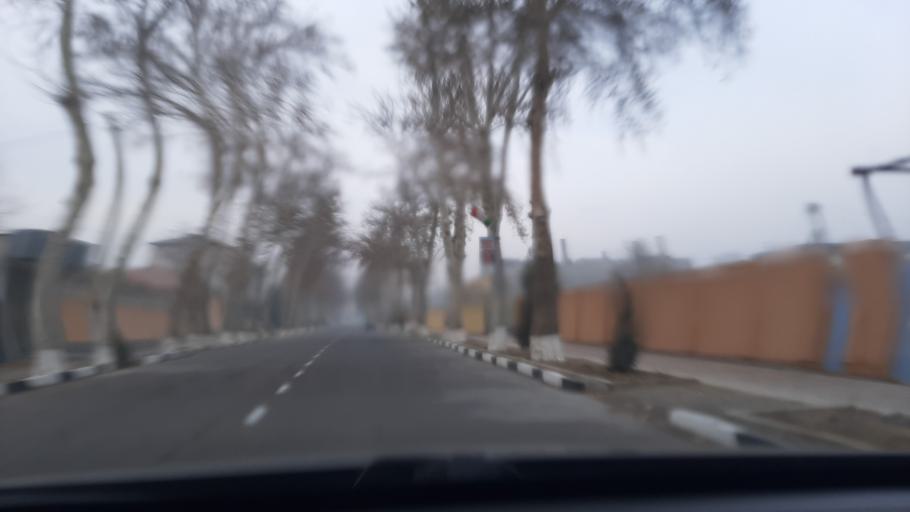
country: TJ
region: Viloyati Sughd
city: Chkalov
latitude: 40.2391
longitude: 69.6952
